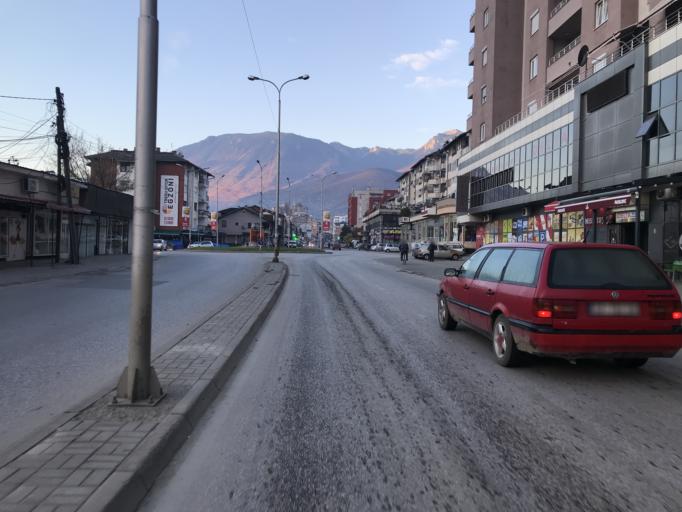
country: XK
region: Pec
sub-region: Komuna e Pejes
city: Peje
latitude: 42.6671
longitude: 20.3027
